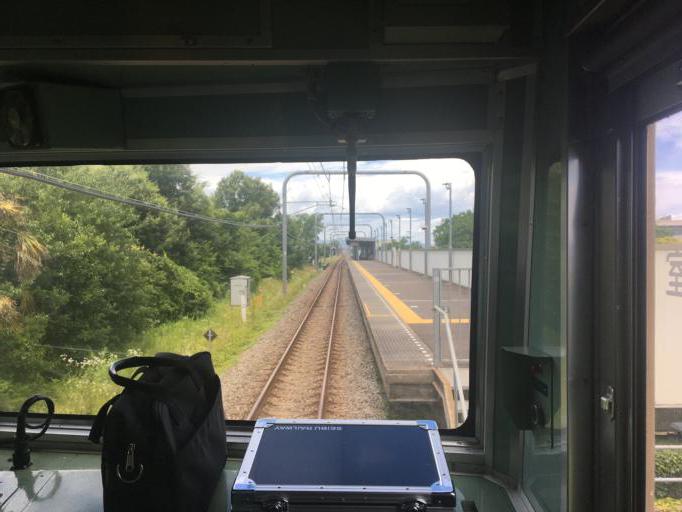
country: JP
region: Tokyo
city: Higashimurayama-shi
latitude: 35.7445
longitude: 139.4688
